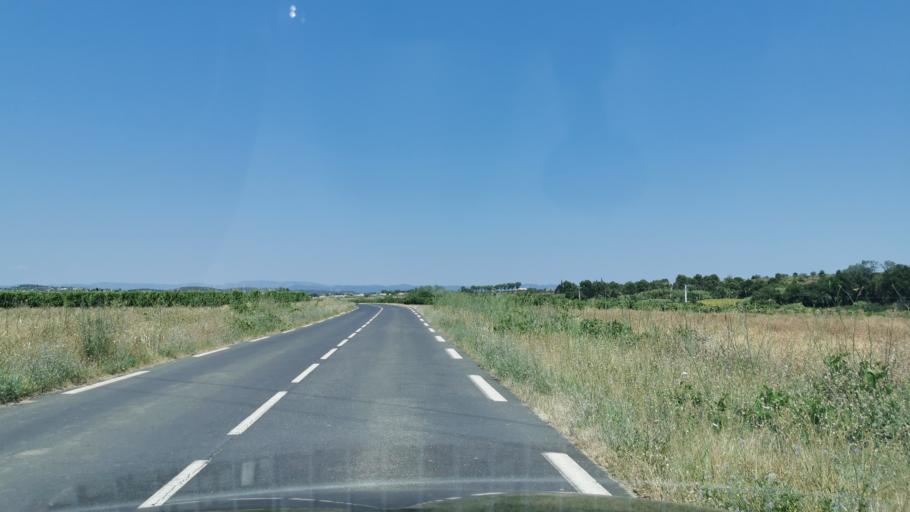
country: FR
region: Languedoc-Roussillon
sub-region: Departement de l'Herault
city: Maureilhan
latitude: 43.3724
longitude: 3.1132
